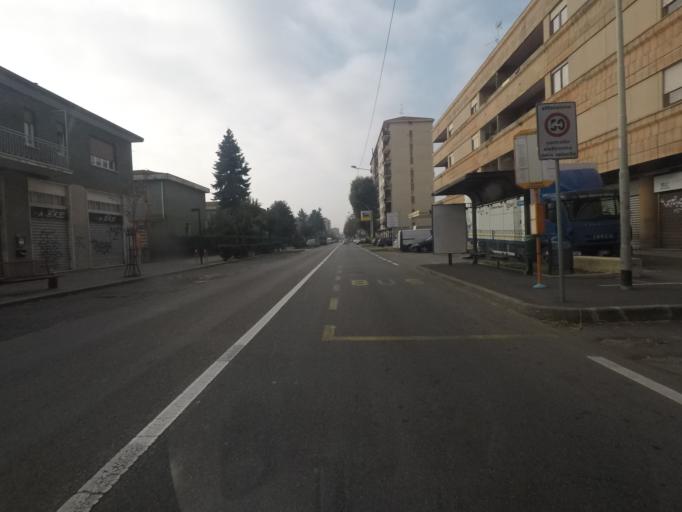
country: IT
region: Lombardy
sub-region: Citta metropolitana di Milano
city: Cologno Monzese
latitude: 45.5348
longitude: 9.2836
